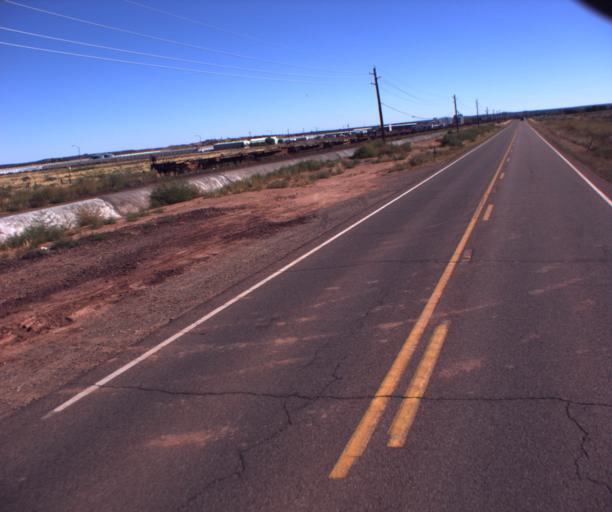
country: US
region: Arizona
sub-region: Navajo County
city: Snowflake
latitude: 34.5131
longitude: -110.1138
